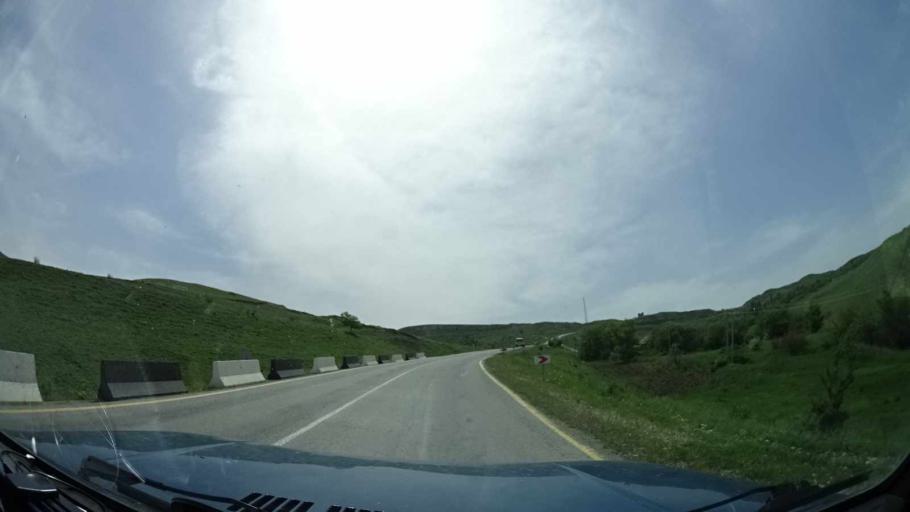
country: AZ
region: Xizi
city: Khyzy
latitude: 40.9054
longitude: 49.1209
